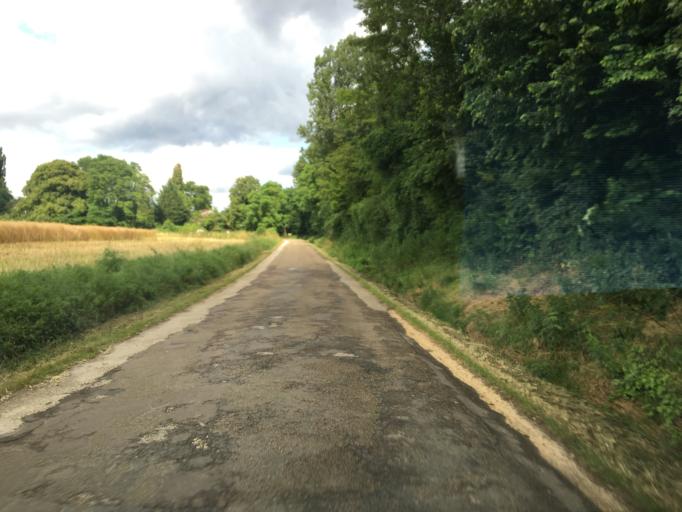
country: FR
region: Bourgogne
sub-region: Departement de l'Yonne
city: Charbuy
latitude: 47.8238
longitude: 3.4365
